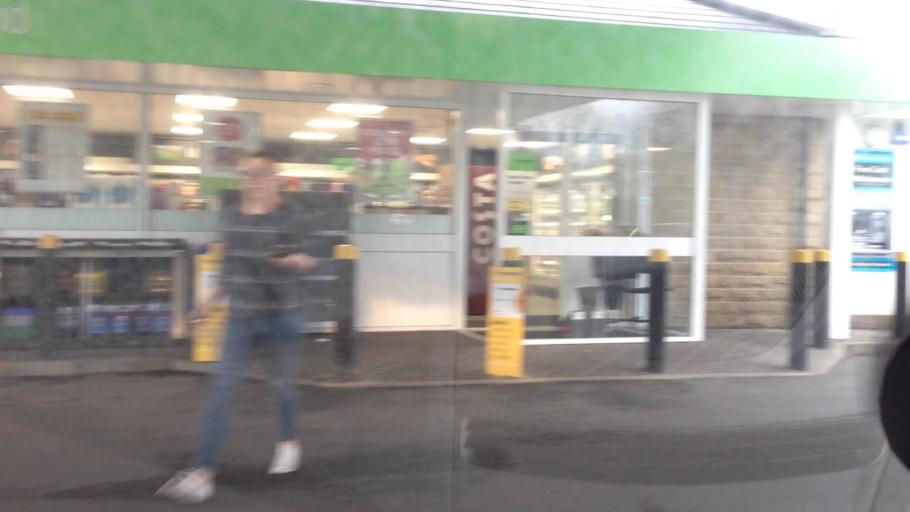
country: GB
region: England
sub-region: Calderdale
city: Elland
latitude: 53.6662
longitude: -1.8220
